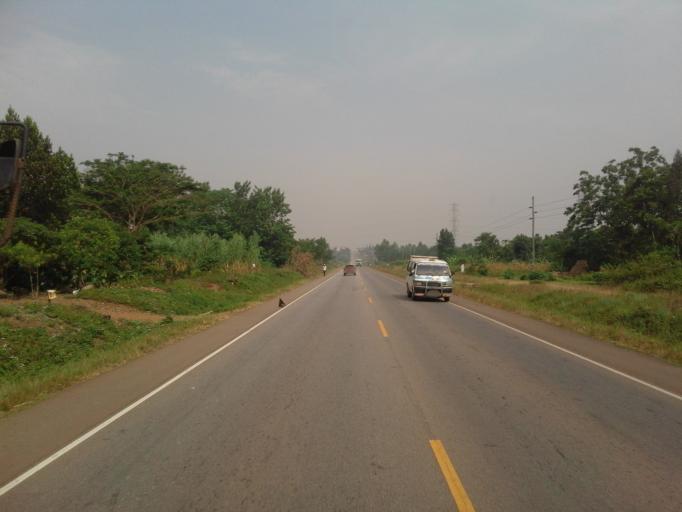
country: UG
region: Eastern Region
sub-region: Bugiri District
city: Bugiri
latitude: 0.5426
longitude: 33.7761
